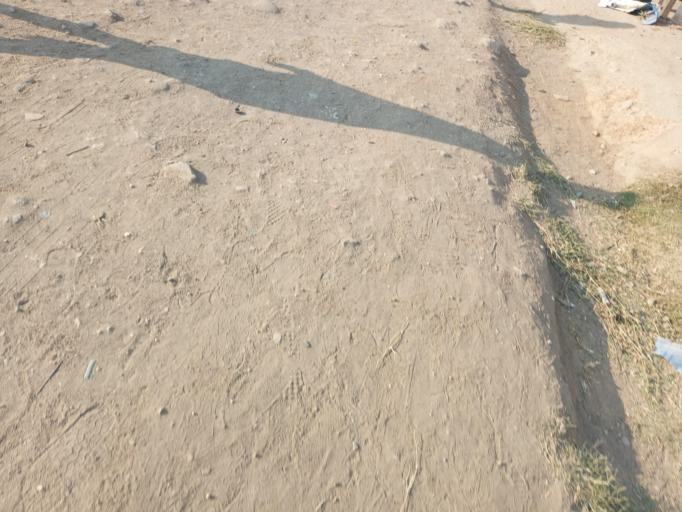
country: ZM
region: Lusaka
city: Lusaka
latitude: -15.3896
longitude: 28.2825
